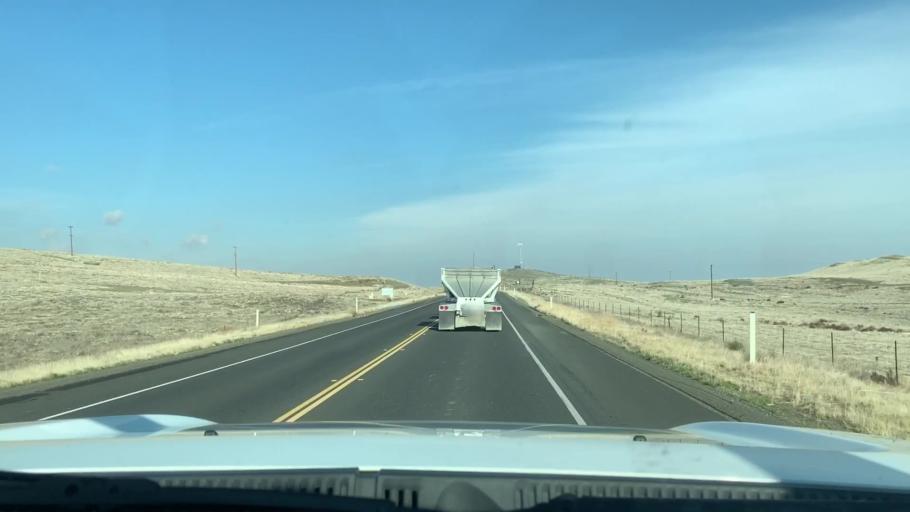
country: US
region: California
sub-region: Fresno County
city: Coalinga
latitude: 36.2161
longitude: -120.3110
